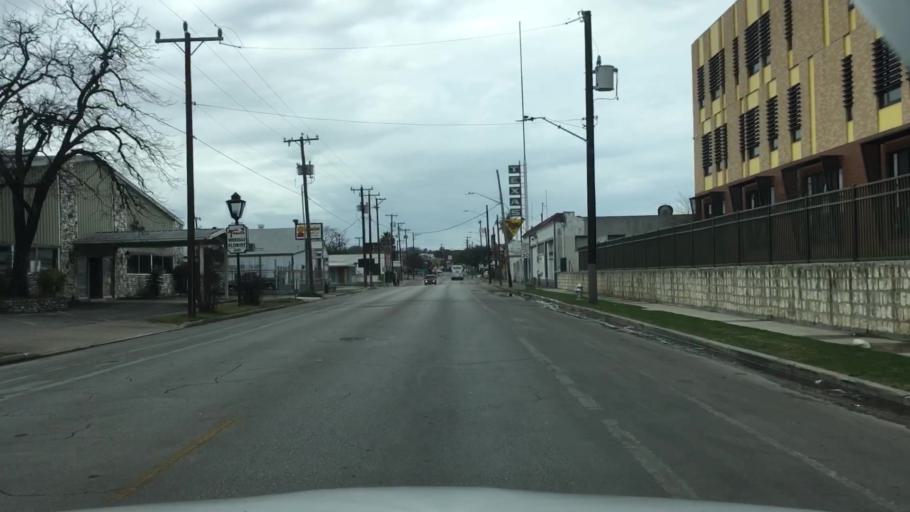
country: US
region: Texas
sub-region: Bexar County
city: San Antonio
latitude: 29.4461
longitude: -98.4836
